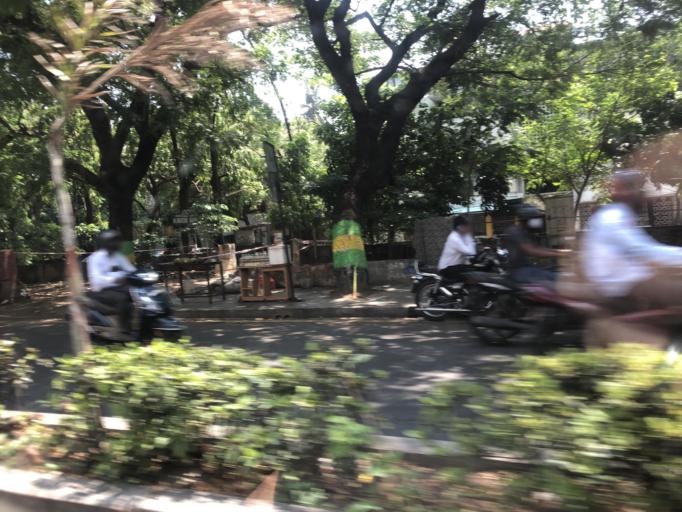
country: IN
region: Tamil Nadu
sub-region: Chennai
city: Gandhi Nagar
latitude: 12.9915
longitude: 80.2560
